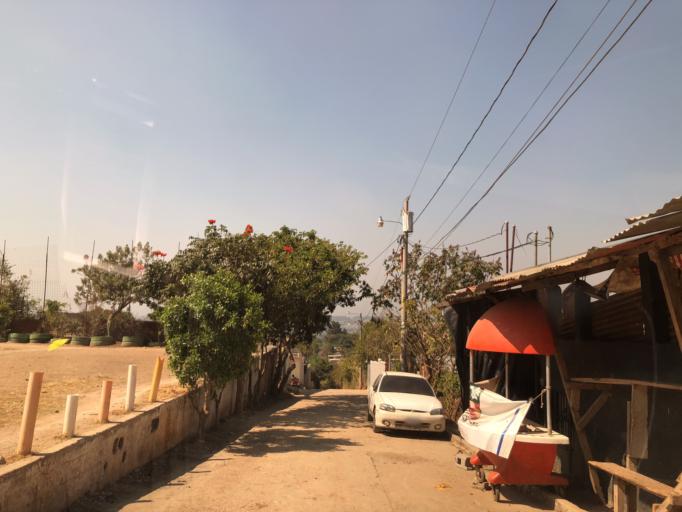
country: GT
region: Guatemala
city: Santa Catarina Pinula
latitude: 14.5368
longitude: -90.5093
